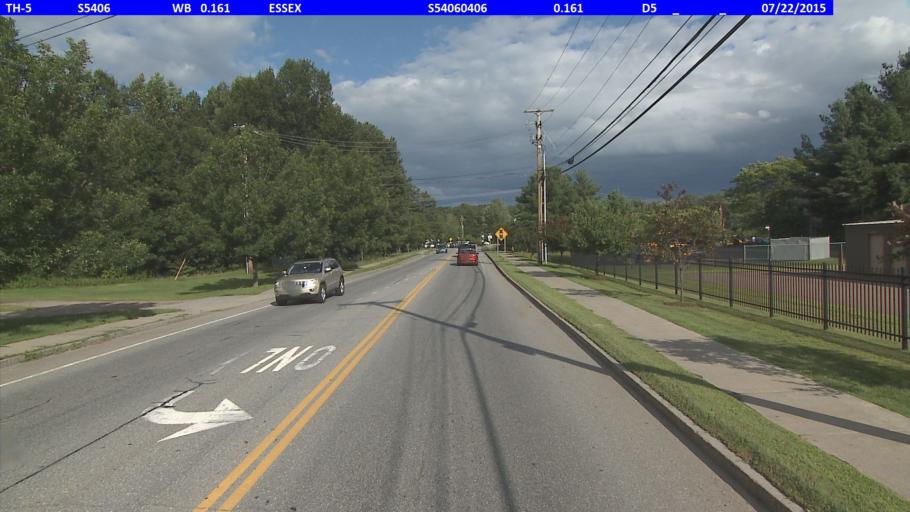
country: US
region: Vermont
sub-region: Chittenden County
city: Essex Junction
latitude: 44.5103
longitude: -73.1346
